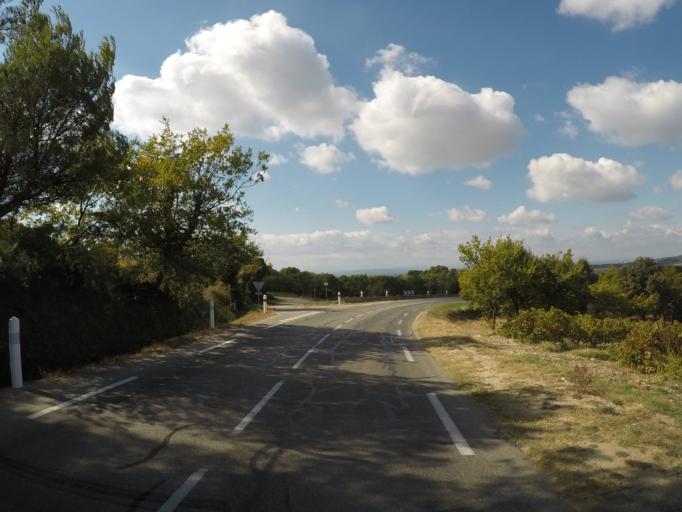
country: FR
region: Provence-Alpes-Cote d'Azur
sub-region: Departement du Vaucluse
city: Visan
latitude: 44.2748
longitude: 5.0003
